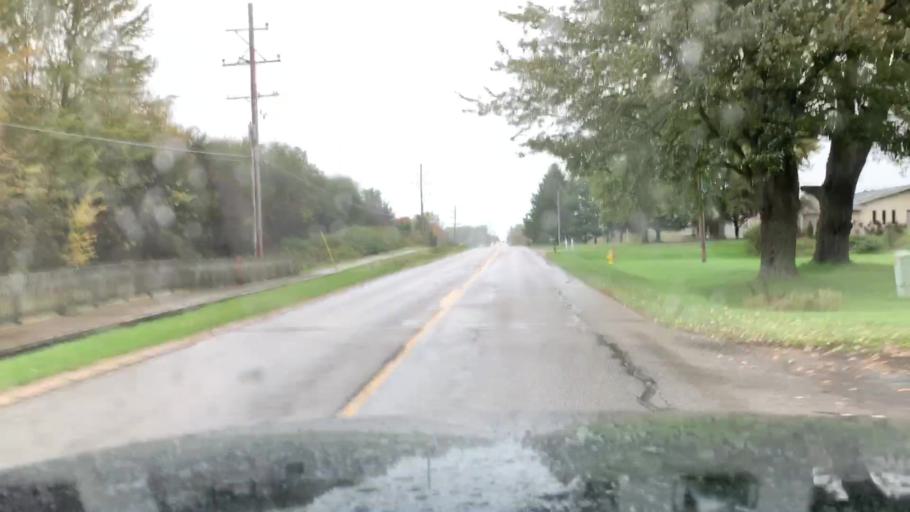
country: US
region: Michigan
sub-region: Ottawa County
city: Holland
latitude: 42.7774
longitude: -86.0577
